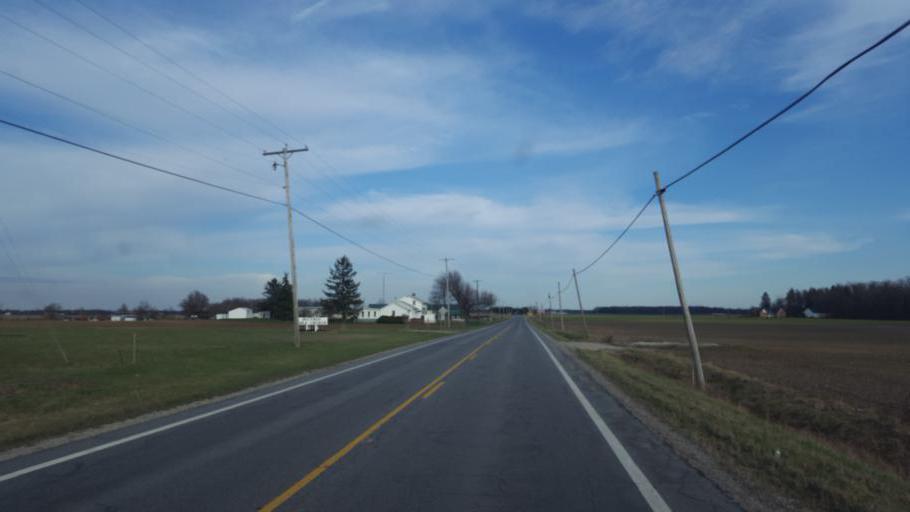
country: US
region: Ohio
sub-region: Crawford County
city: Bucyrus
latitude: 40.7822
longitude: -82.9388
